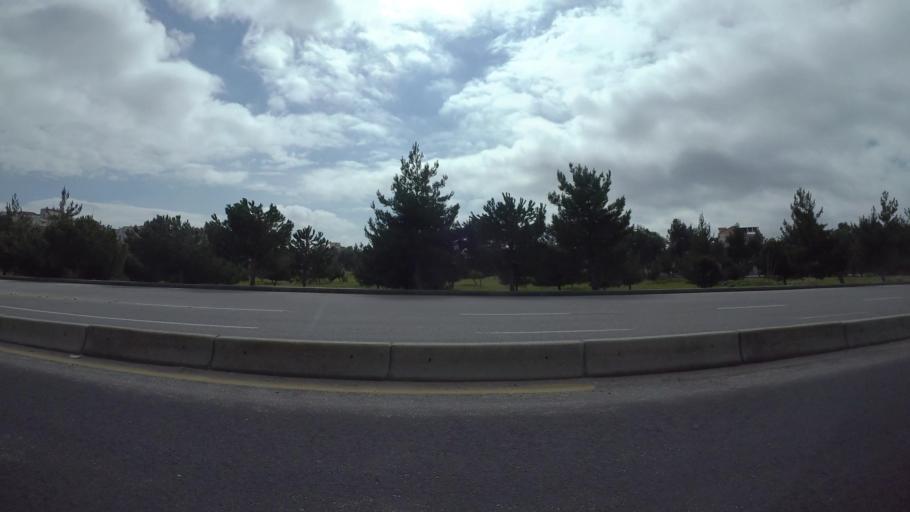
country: JO
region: Amman
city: Wadi as Sir
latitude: 31.9932
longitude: 35.8275
